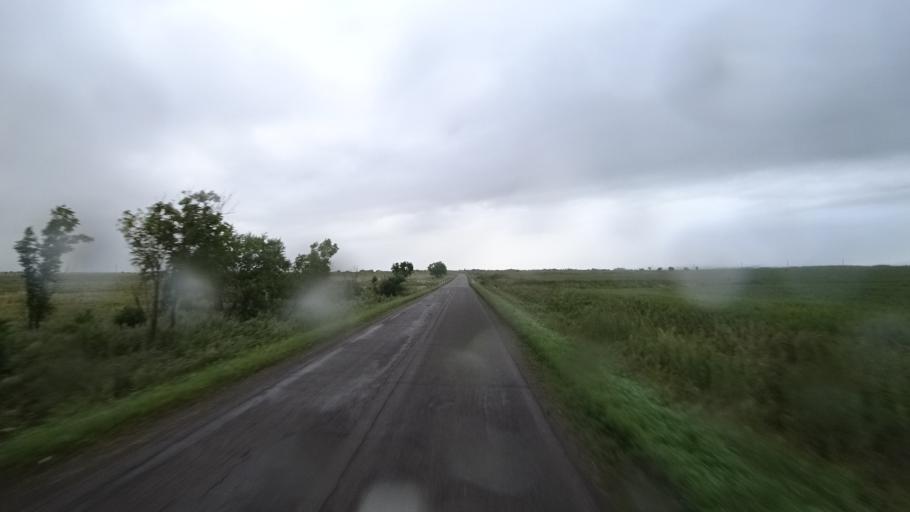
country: RU
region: Primorskiy
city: Chernigovka
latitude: 44.3852
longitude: 132.5295
